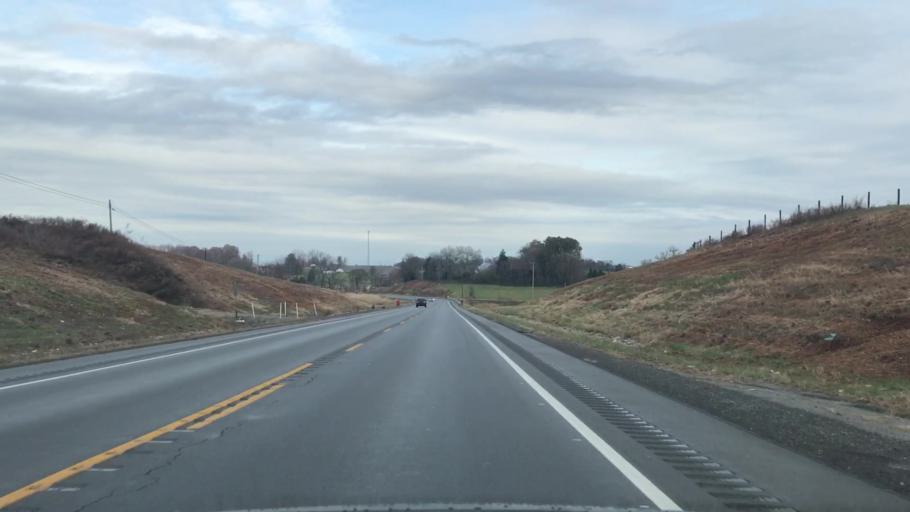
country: US
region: Kentucky
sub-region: Monroe County
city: Tompkinsville
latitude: 36.7756
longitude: -85.6848
